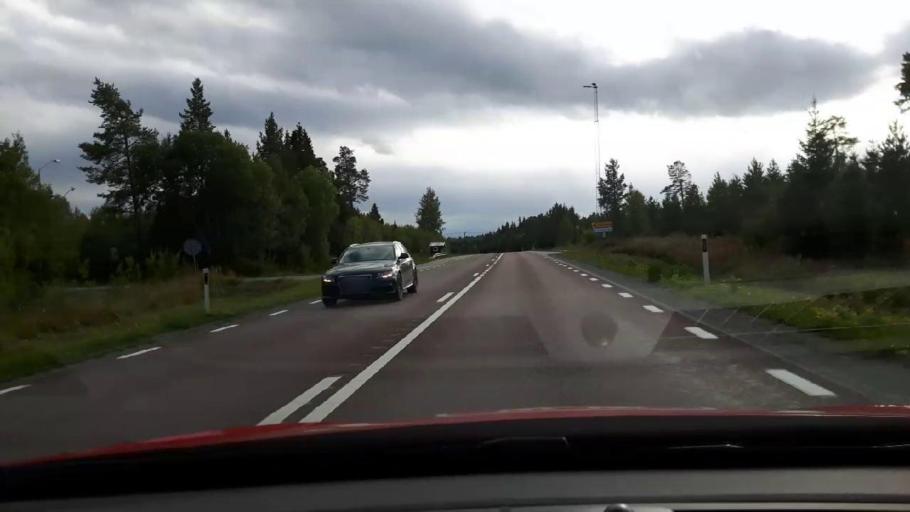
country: SE
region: Jaemtland
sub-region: OEstersunds Kommun
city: Brunflo
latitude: 63.0540
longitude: 14.8290
